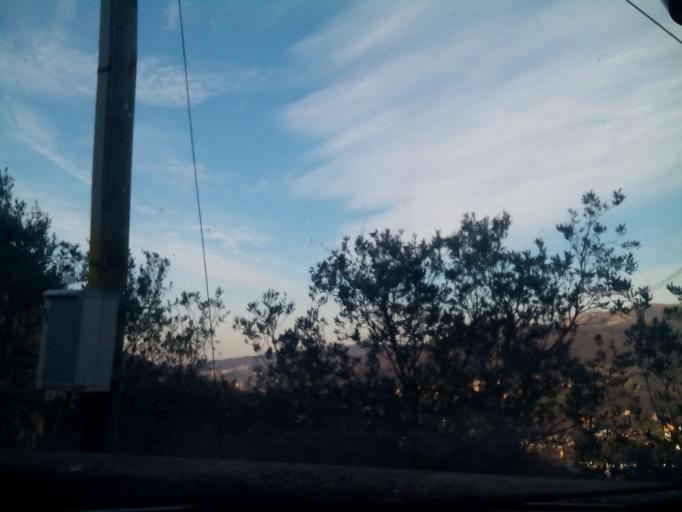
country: IT
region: Liguria
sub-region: Provincia di Genova
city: Piccarello
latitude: 44.4651
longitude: 8.9926
